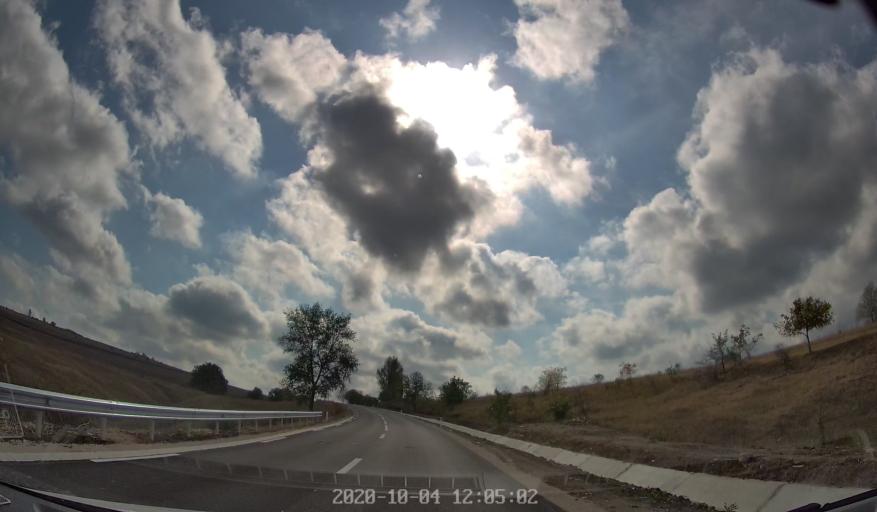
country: MD
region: Rezina
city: Saharna
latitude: 47.5979
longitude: 28.9480
